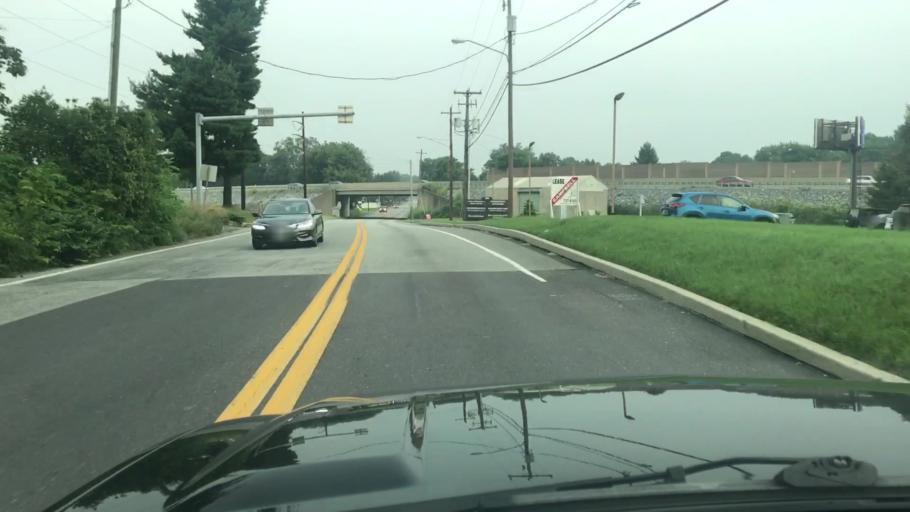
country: US
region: Pennsylvania
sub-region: Cumberland County
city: Shiremanstown
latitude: 40.2320
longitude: -76.9549
